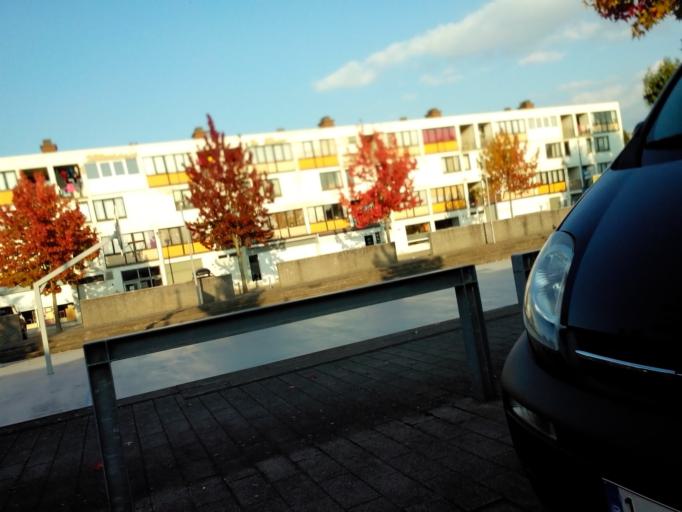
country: BE
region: Flanders
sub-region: Provincie Vlaams-Brabant
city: Leuven
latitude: 50.8791
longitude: 4.7289
